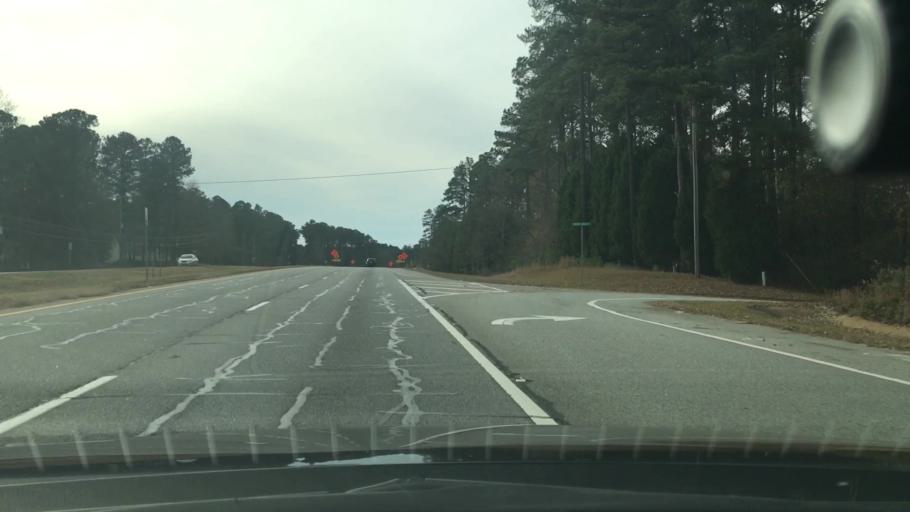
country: US
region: Georgia
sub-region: Fayette County
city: Peachtree City
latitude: 33.4008
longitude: -84.6499
